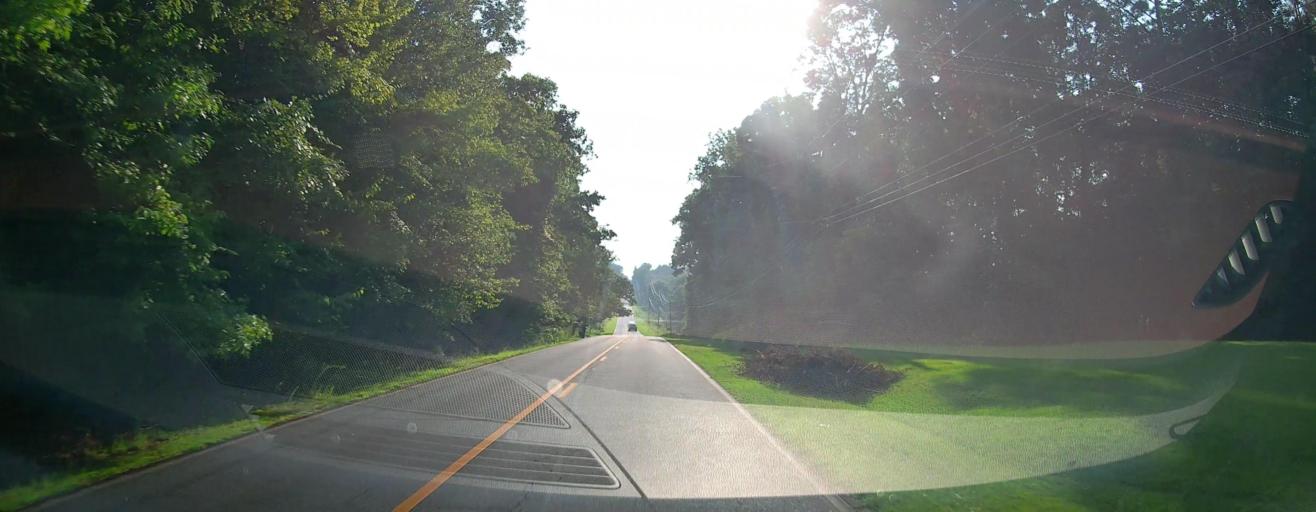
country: US
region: Georgia
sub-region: Bibb County
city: West Point
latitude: 32.8316
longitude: -83.7931
